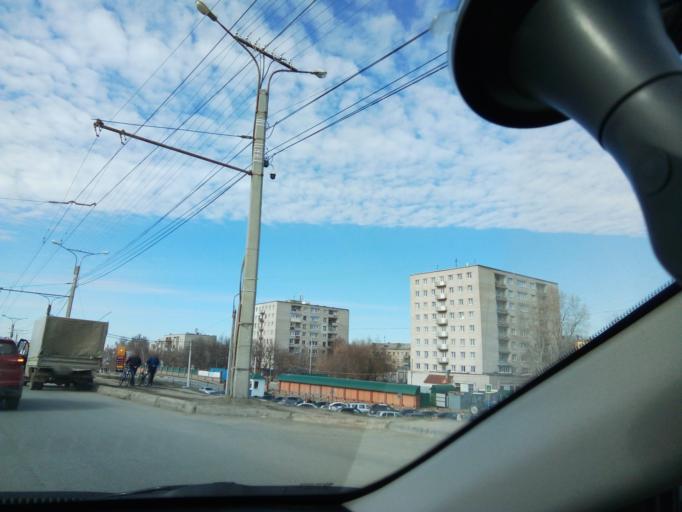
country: RU
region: Chuvashia
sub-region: Cheboksarskiy Rayon
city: Cheboksary
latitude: 56.1228
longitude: 47.2460
